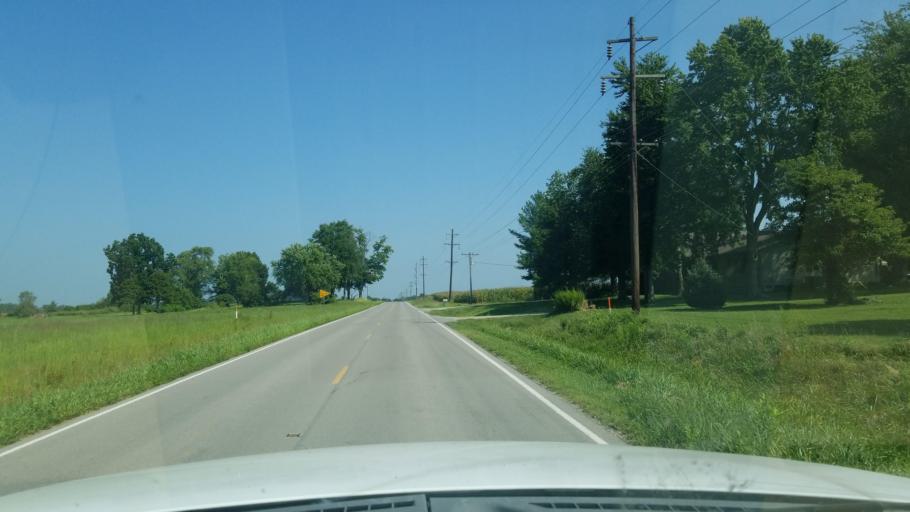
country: US
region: Illinois
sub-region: Saline County
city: Harrisburg
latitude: 37.8751
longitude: -88.6055
